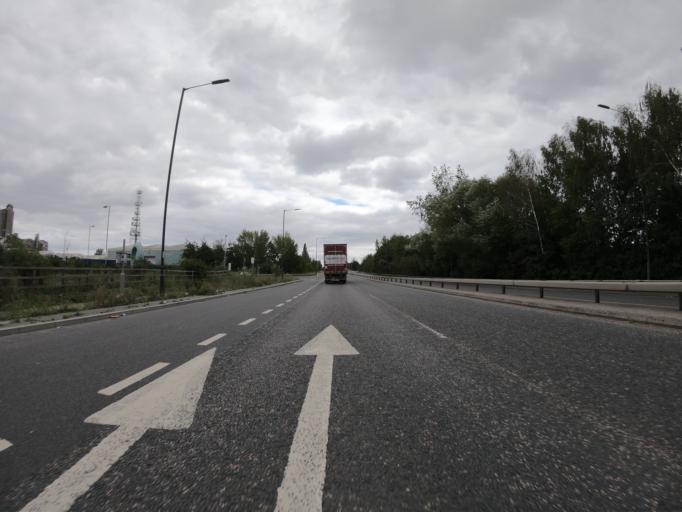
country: GB
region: England
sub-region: Greater London
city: Belvedere
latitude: 51.4927
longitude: 0.1626
